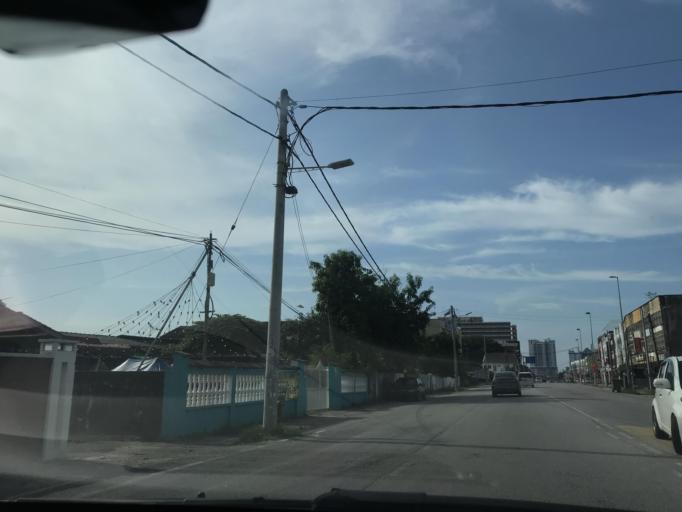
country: MY
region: Kelantan
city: Kota Bharu
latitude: 6.1183
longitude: 102.2471
